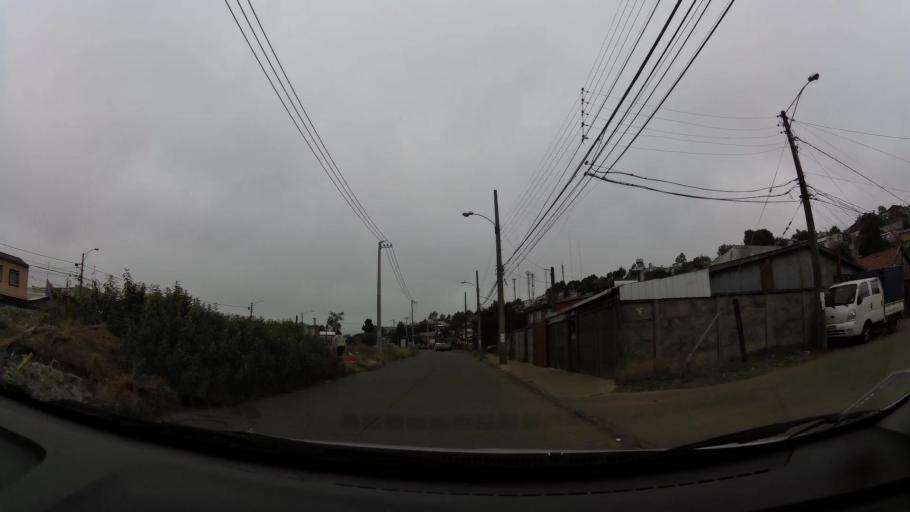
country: CL
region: Biobio
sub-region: Provincia de Concepcion
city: Concepcion
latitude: -36.8098
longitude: -73.0416
